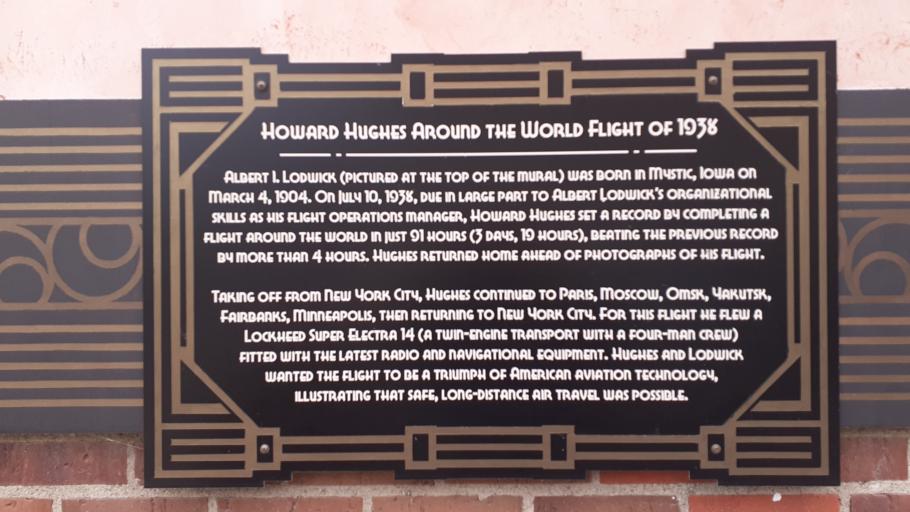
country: US
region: Iowa
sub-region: Appanoose County
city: Centerville
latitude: 40.7343
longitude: -92.8752
